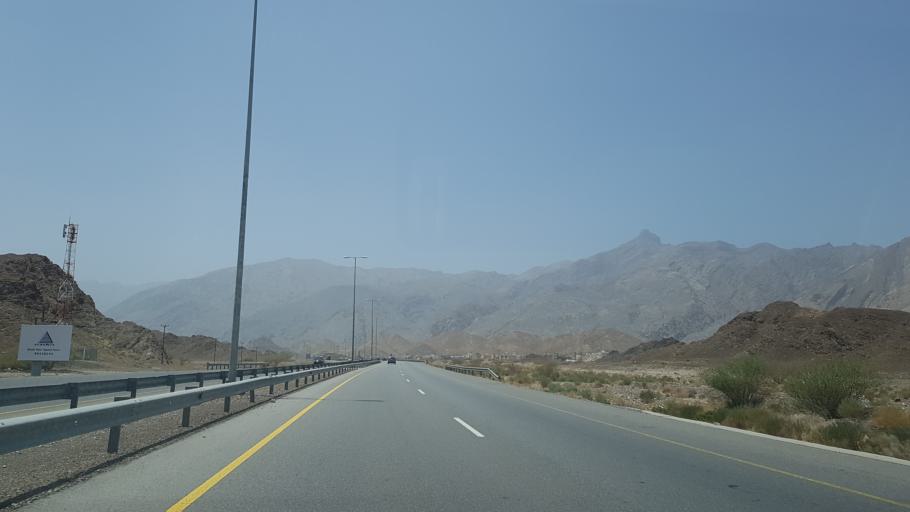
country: OM
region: Muhafazat ad Dakhiliyah
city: Sufalat Sama'il
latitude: 23.3270
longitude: 57.9712
